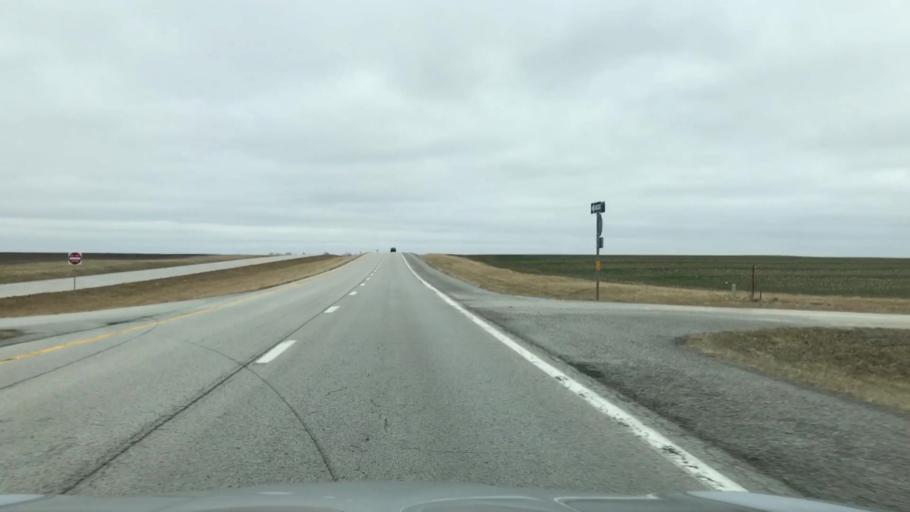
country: US
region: Missouri
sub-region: Livingston County
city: Chillicothe
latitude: 39.7761
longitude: -93.4823
